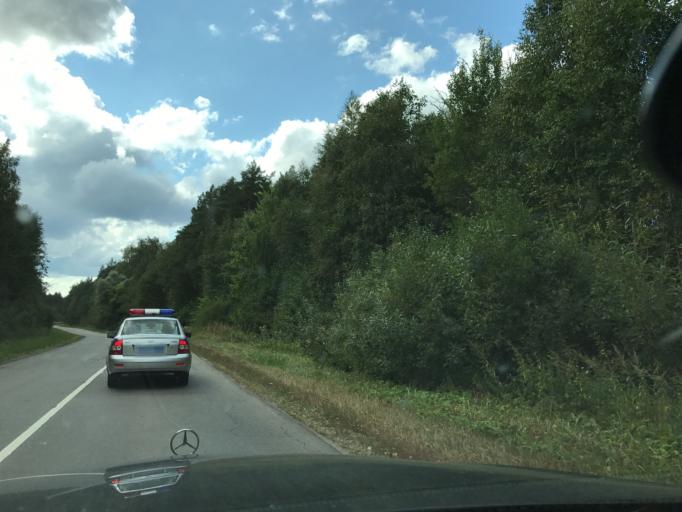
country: RU
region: Vladimir
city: Vorsha
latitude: 56.0081
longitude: 40.0953
